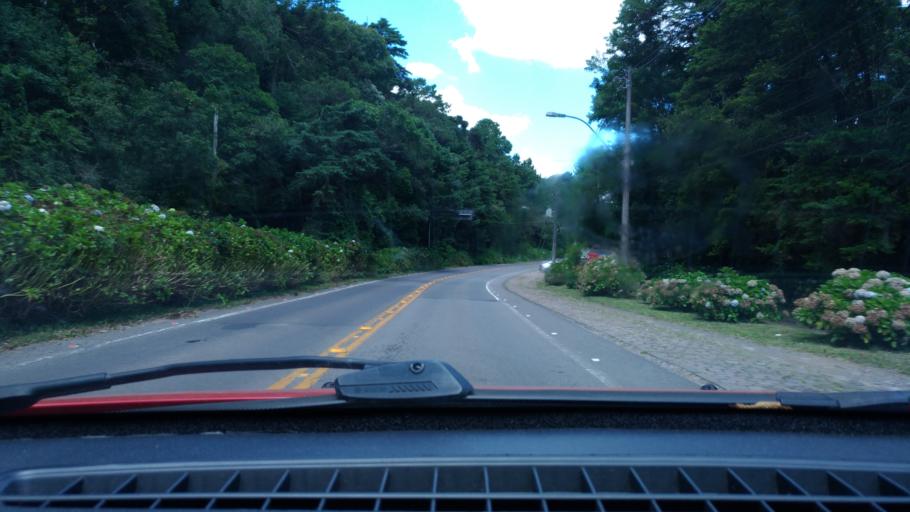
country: BR
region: Rio Grande do Sul
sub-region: Canela
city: Canela
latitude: -29.3563
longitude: -50.8292
